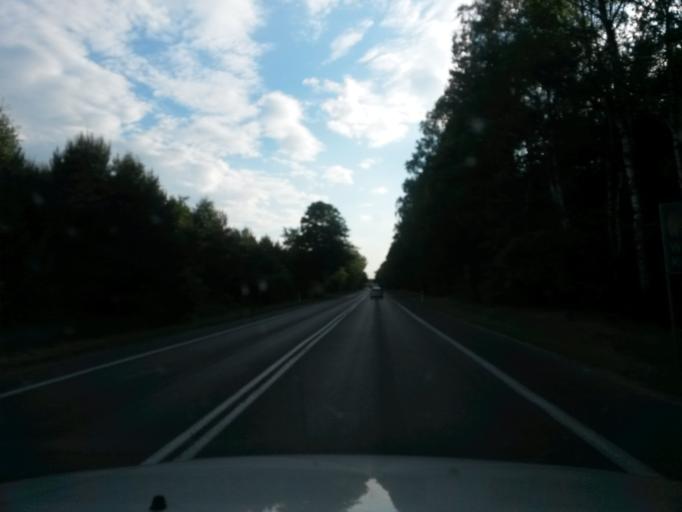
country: PL
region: Lodz Voivodeship
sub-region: Powiat belchatowski
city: Belchatow
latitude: 51.3533
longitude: 19.3281
